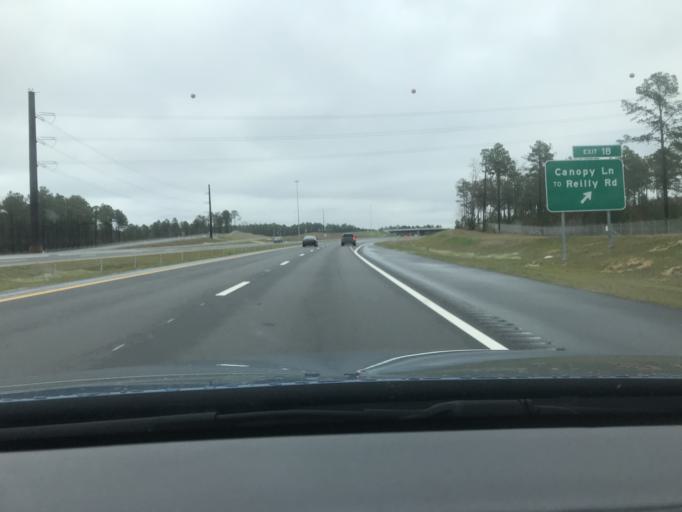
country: US
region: North Carolina
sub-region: Cumberland County
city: Fort Bragg
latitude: 35.1039
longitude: -79.0191
